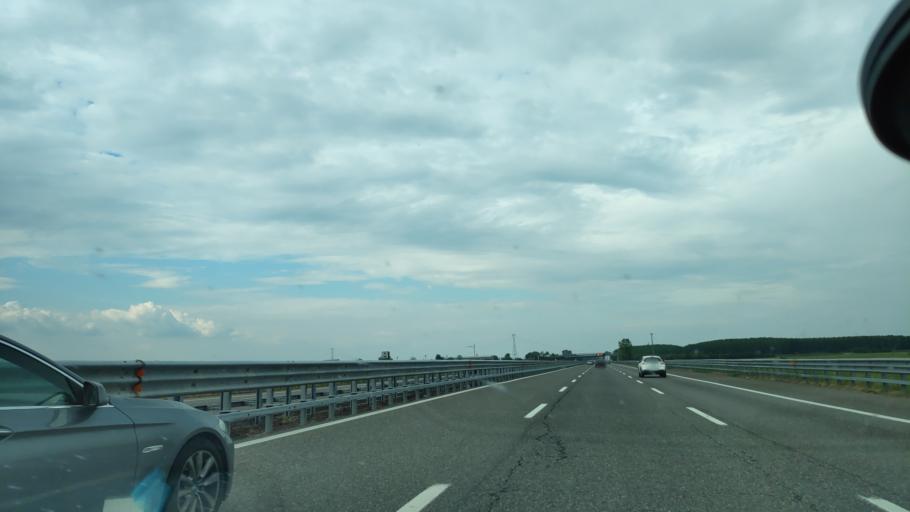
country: IT
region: Lombardy
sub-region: Provincia di Pavia
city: Corana
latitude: 45.0573
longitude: 8.9546
